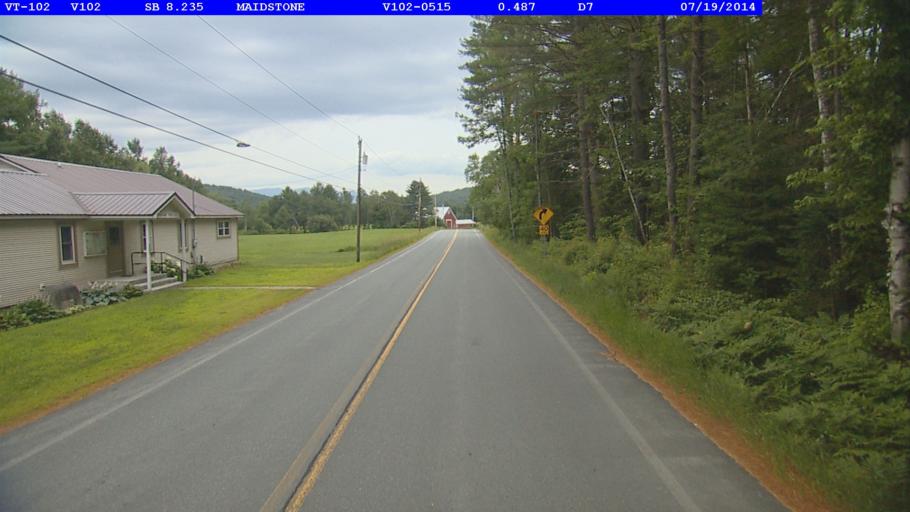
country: US
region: Vermont
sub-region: Essex County
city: Guildhall
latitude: 44.5777
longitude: -71.5550
